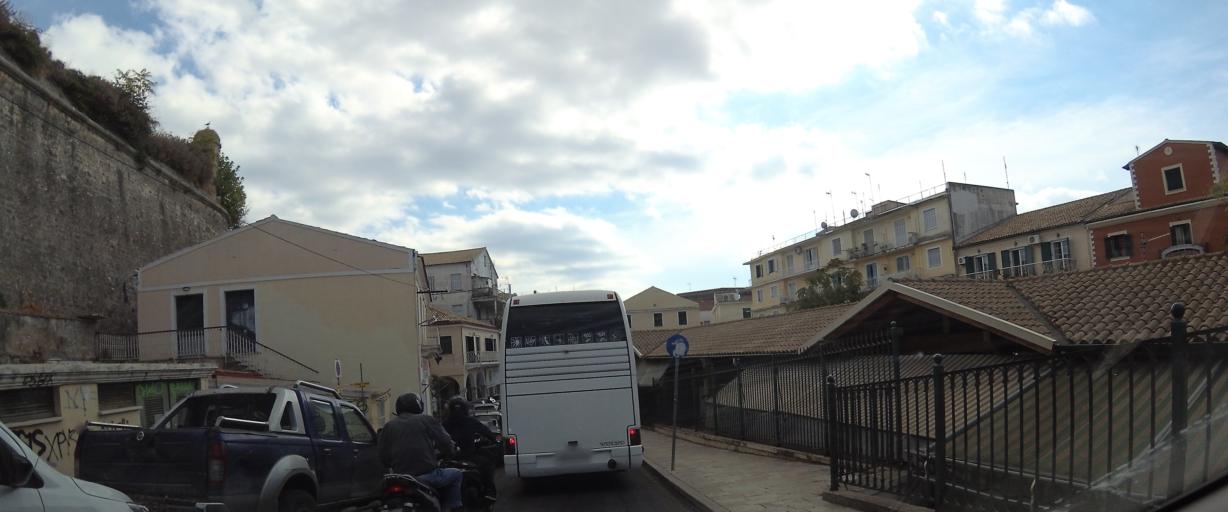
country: GR
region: Ionian Islands
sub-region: Nomos Kerkyras
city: Kerkyra
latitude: 39.6231
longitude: 19.9183
